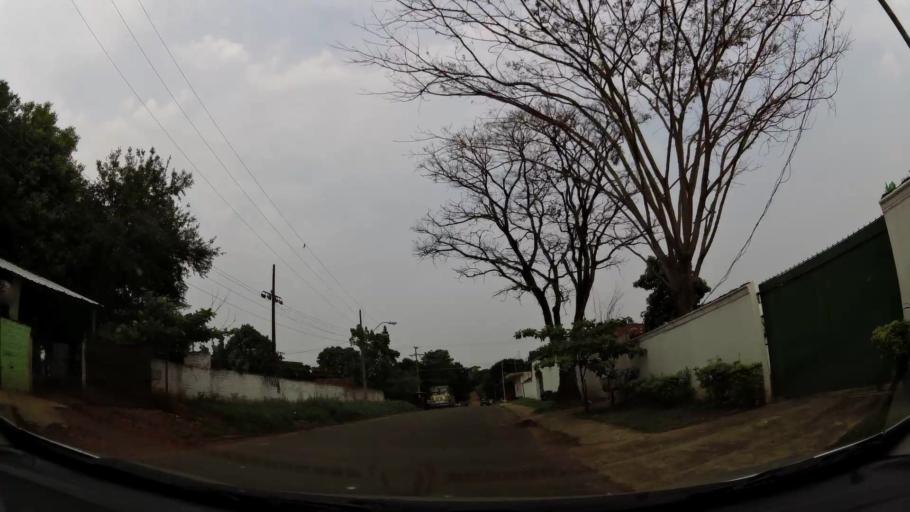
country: BR
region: Parana
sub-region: Foz Do Iguacu
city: Foz do Iguacu
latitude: -25.5621
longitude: -54.6039
